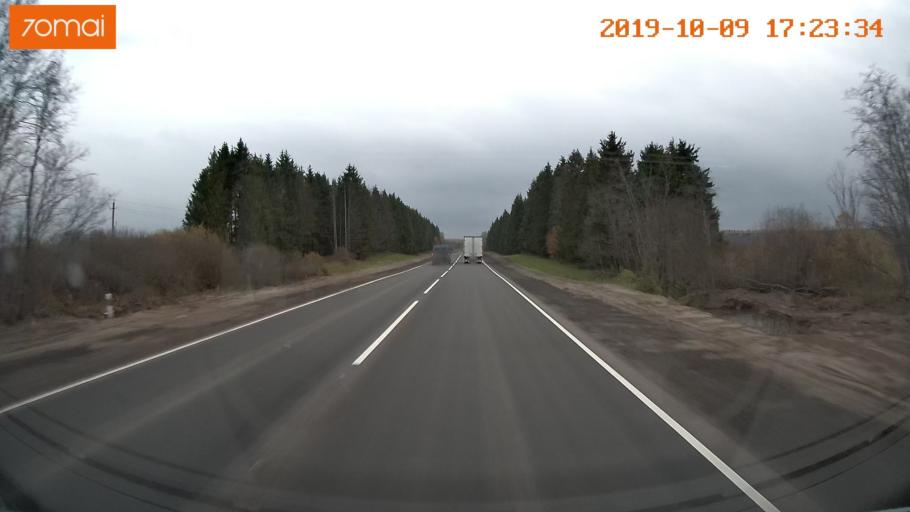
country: RU
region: Ivanovo
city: Furmanov
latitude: 57.1949
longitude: 41.1157
